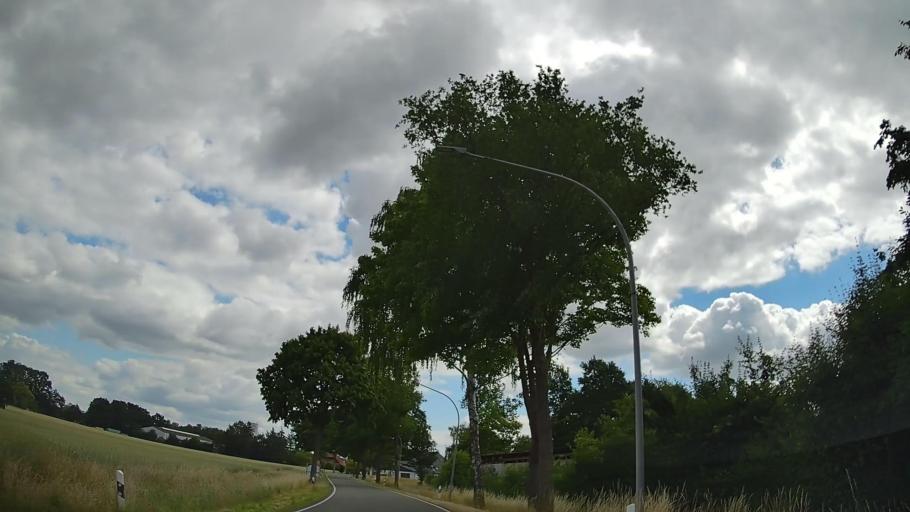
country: DE
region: Lower Saxony
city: Brockum
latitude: 52.4517
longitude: 8.4859
